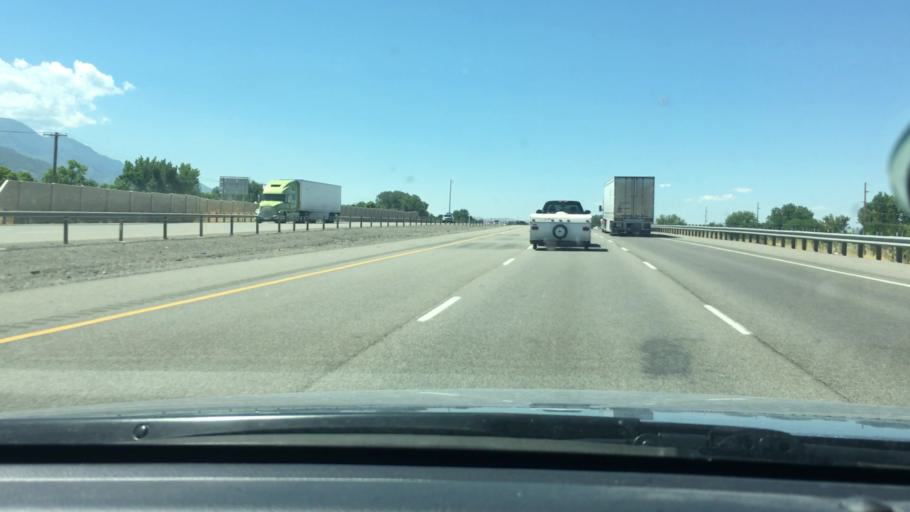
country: US
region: Utah
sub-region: Utah County
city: Payson
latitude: 40.0480
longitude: -111.7379
